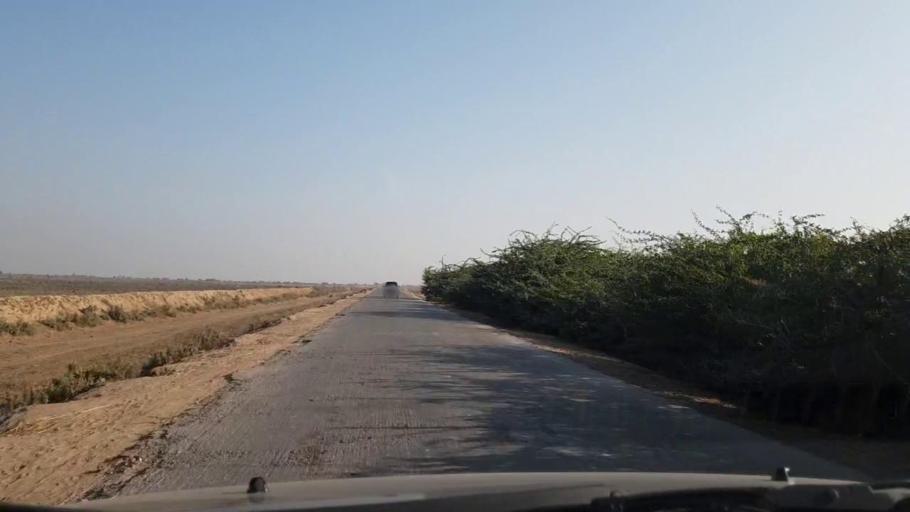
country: PK
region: Sindh
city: Tando Bago
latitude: 24.8084
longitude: 68.9921
